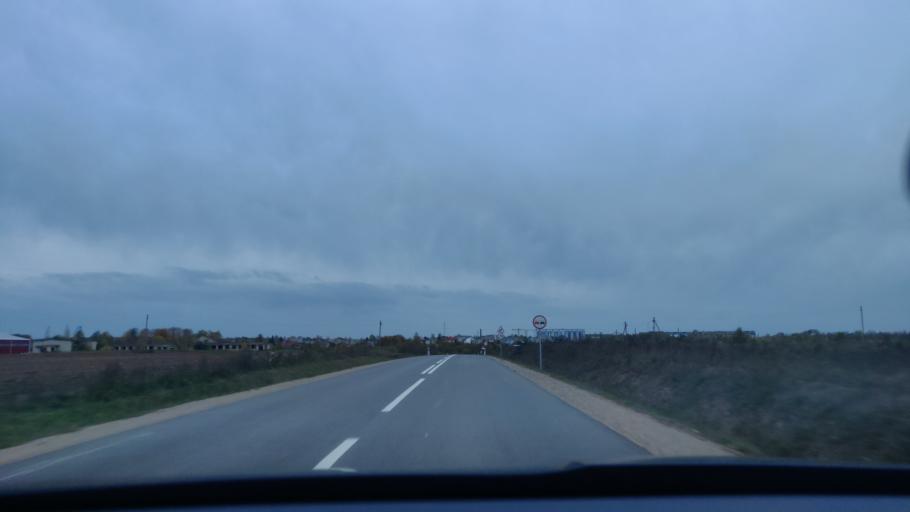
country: LT
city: Lentvaris
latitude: 54.6064
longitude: 24.9974
